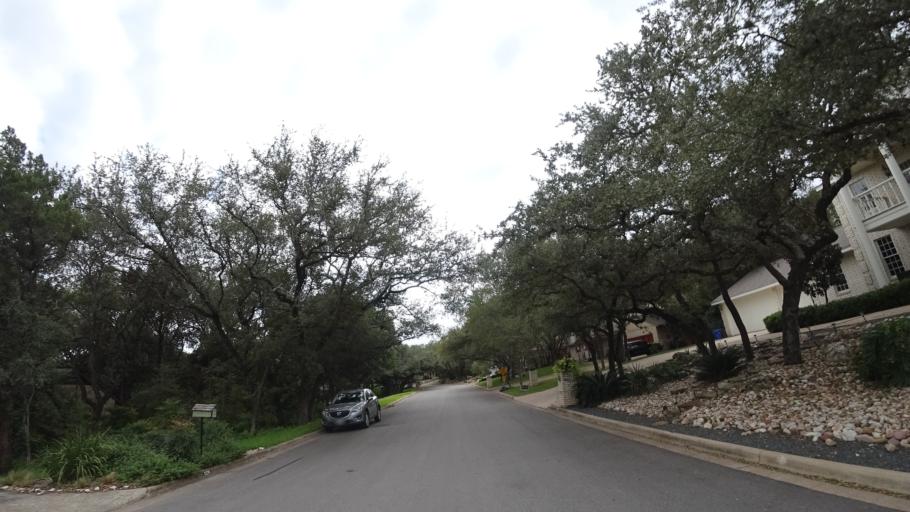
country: US
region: Texas
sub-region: Travis County
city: Rollingwood
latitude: 30.2786
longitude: -97.7890
